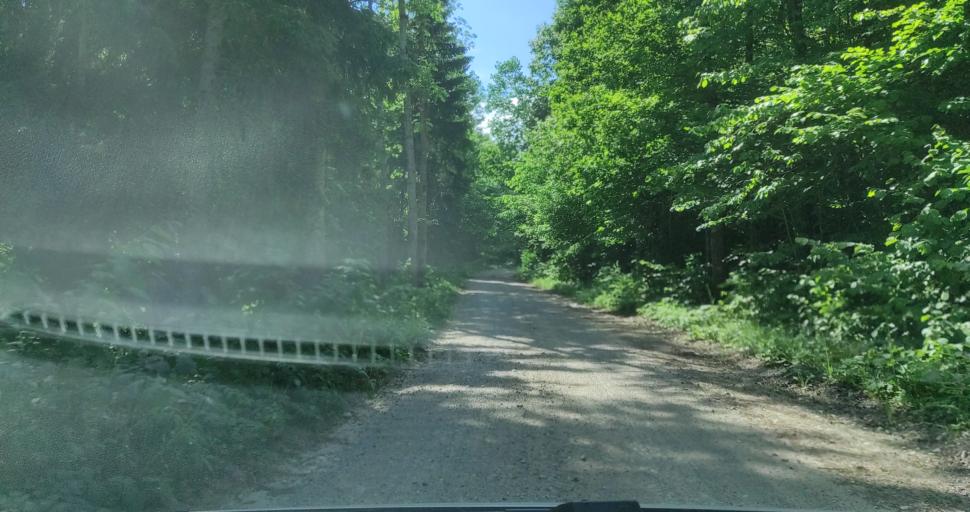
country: LV
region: Kuldigas Rajons
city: Kuldiga
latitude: 56.8478
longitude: 21.9260
